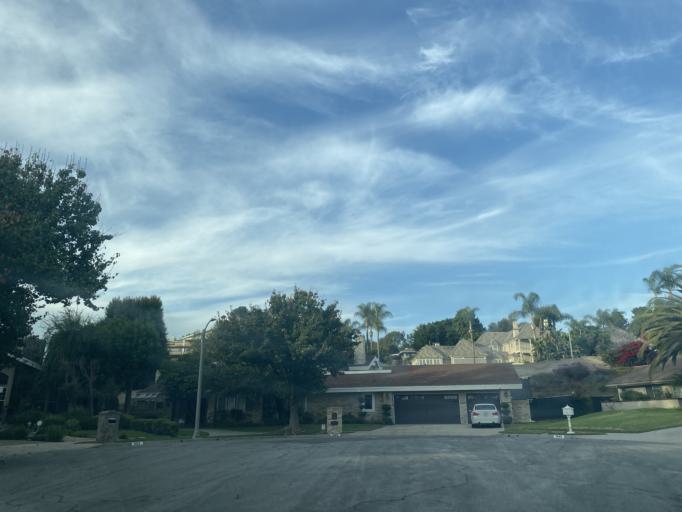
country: US
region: California
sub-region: Orange County
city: Brea
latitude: 33.8882
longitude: -117.8958
